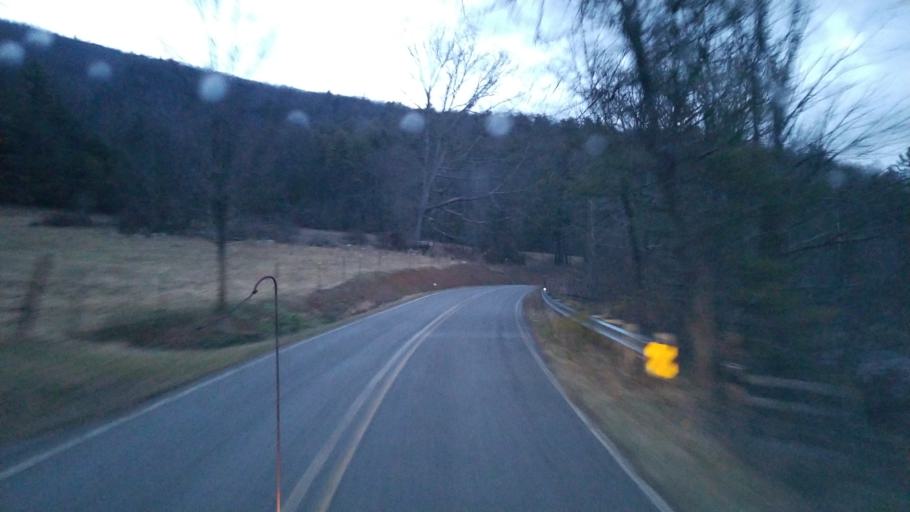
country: US
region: Virginia
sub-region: Pulaski County
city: Pulaski
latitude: 37.1364
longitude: -80.8516
